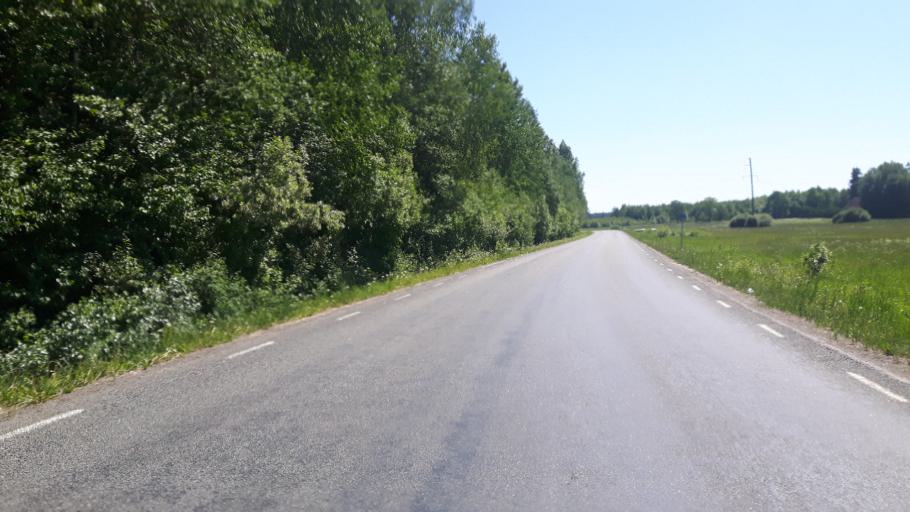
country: EE
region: Raplamaa
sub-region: Kohila vald
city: Kohila
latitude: 59.2061
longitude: 24.6879
